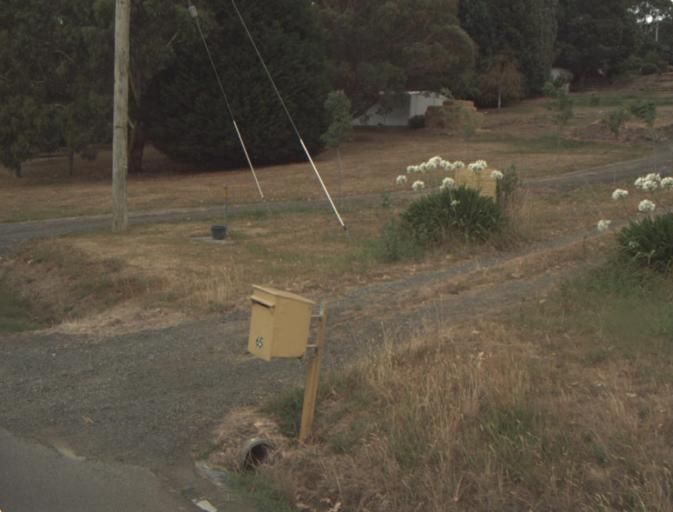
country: AU
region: Tasmania
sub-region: Launceston
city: Mayfield
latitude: -41.3274
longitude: 147.0658
